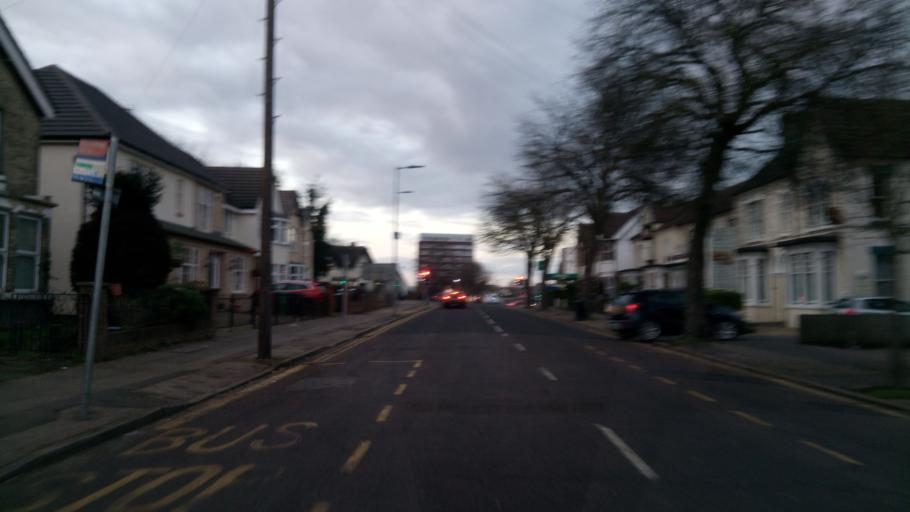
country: GB
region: England
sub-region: Peterborough
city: Peterborough
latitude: 52.5631
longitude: -0.2422
